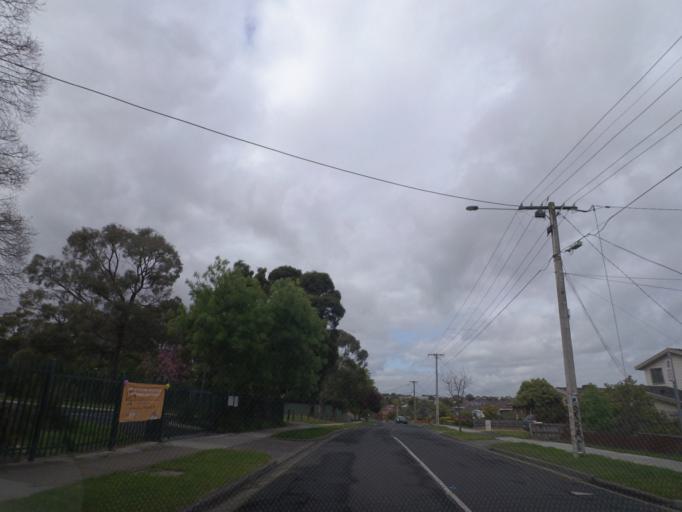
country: AU
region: Victoria
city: Mitcham
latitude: -37.8098
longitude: 145.1895
